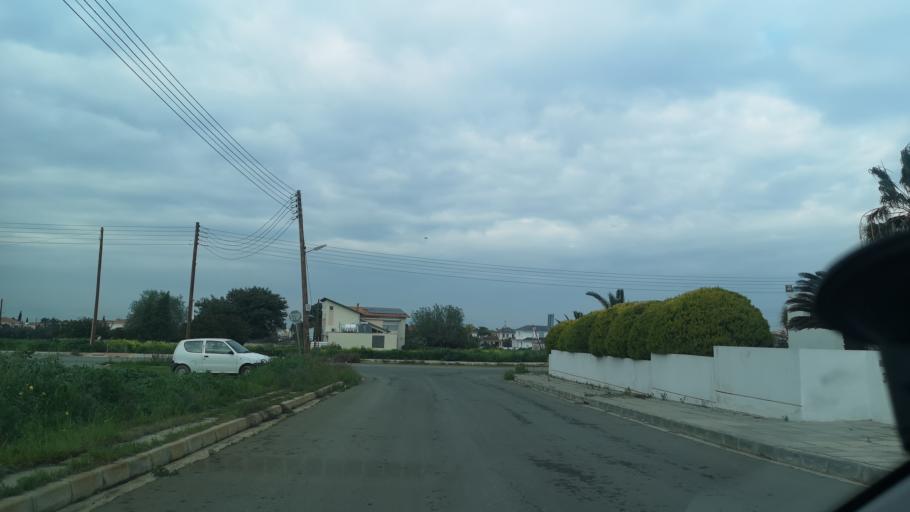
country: CY
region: Lefkosia
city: Kato Deftera
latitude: 35.0844
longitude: 33.2876
